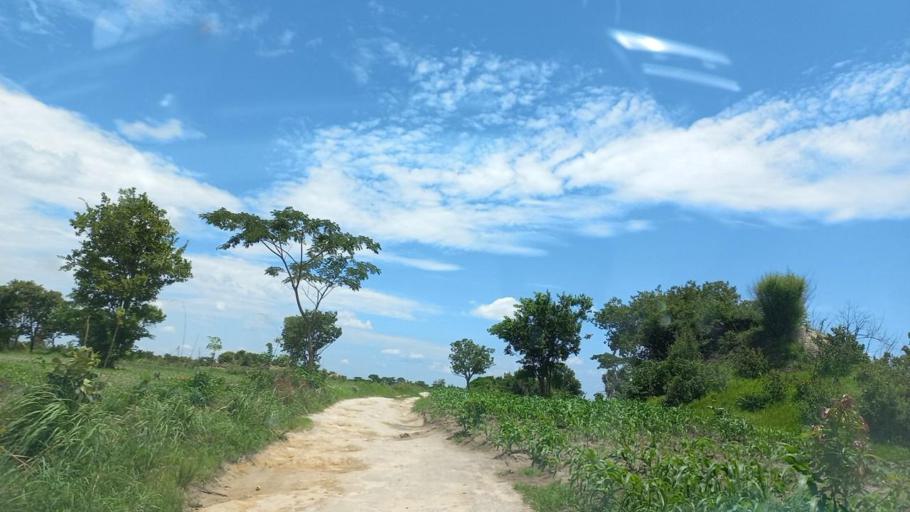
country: ZM
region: Copperbelt
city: Ndola
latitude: -12.8684
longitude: 28.4363
